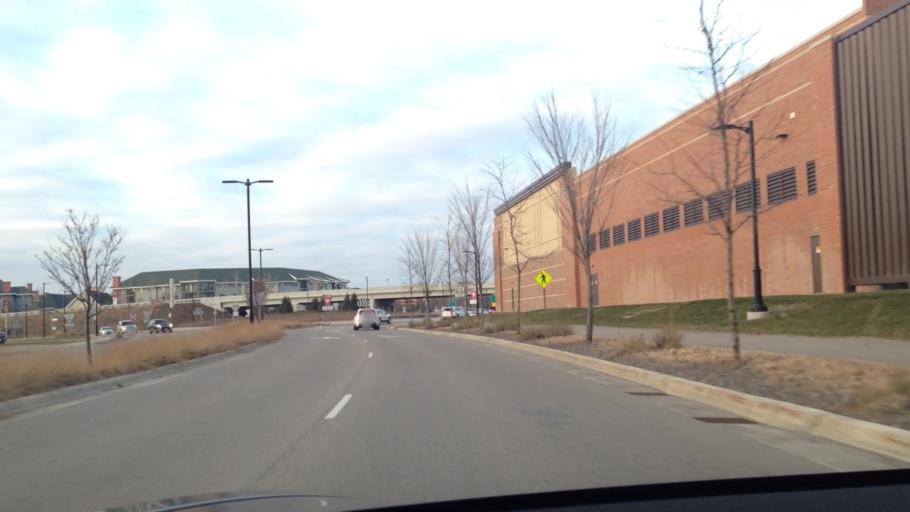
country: US
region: Minnesota
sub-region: Hennepin County
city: Saint Louis Park
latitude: 44.9360
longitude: -93.3684
